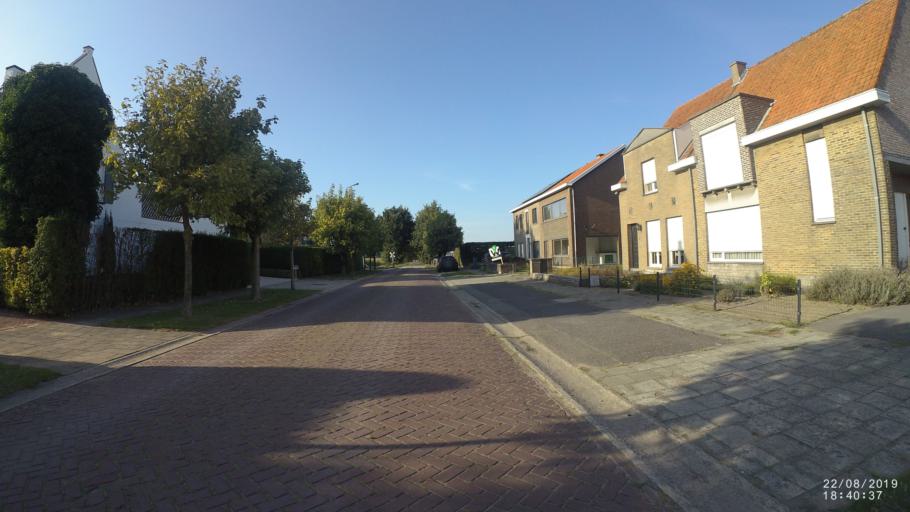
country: BE
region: Flanders
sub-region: Provincie Oost-Vlaanderen
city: Eeklo
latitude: 51.1928
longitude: 3.5549
